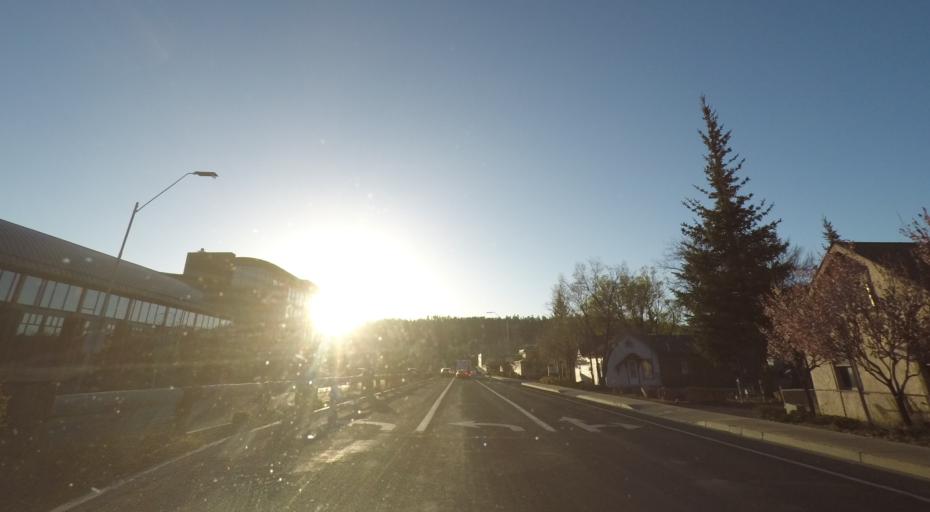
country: US
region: Arizona
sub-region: Coconino County
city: Flagstaff
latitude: 35.1947
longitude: -111.6533
